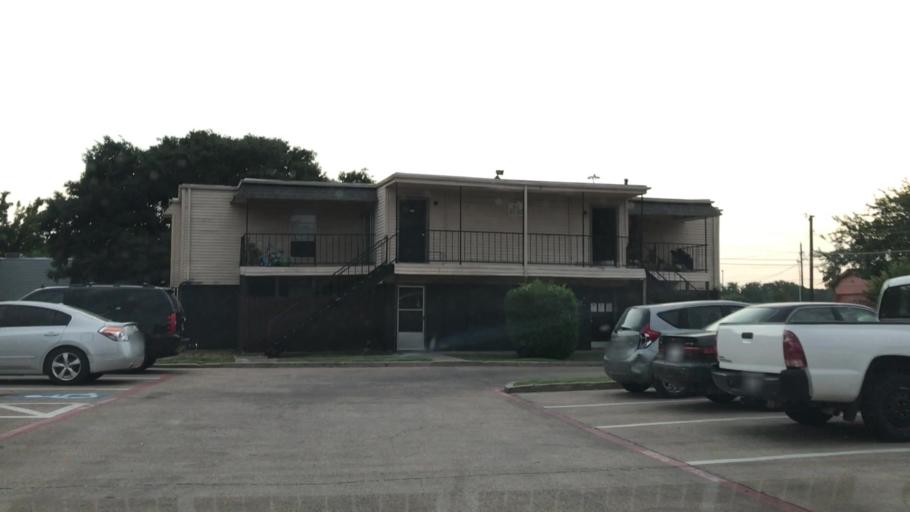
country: US
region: Texas
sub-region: Dallas County
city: Highland Park
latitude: 32.7914
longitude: -96.7107
